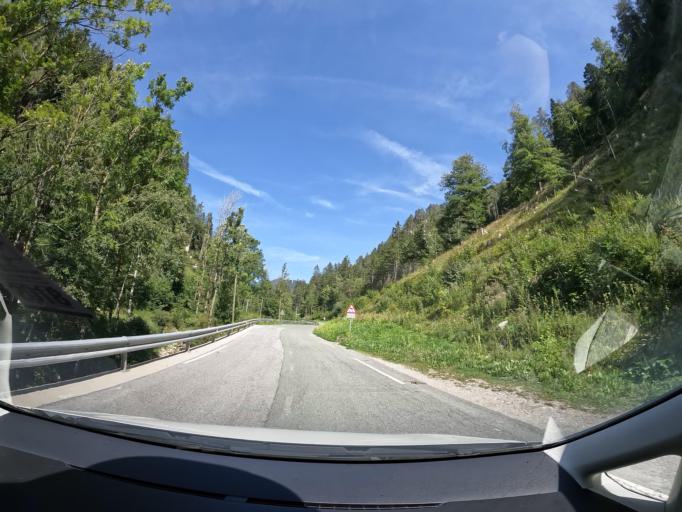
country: SI
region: Jesenice
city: Koroska Bela
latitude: 46.4738
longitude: 14.1045
